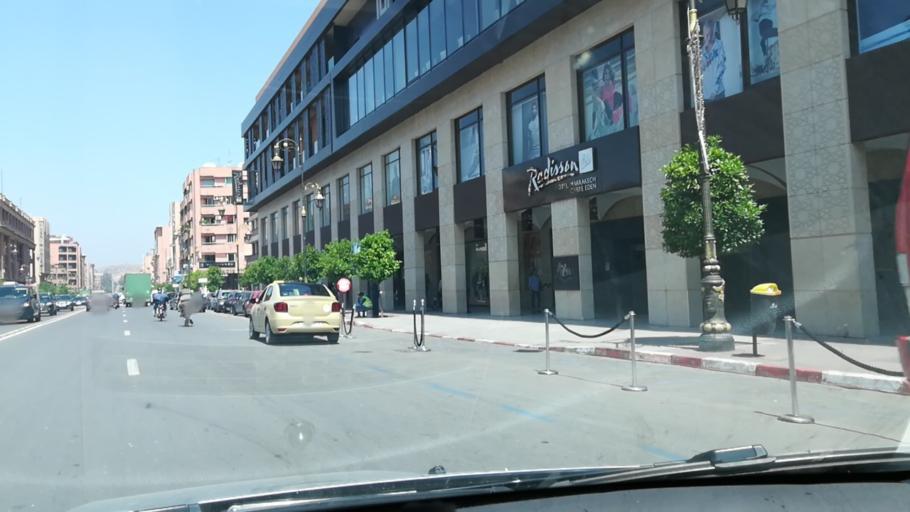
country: MA
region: Marrakech-Tensift-Al Haouz
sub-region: Marrakech
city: Marrakesh
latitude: 31.6344
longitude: -8.0116
